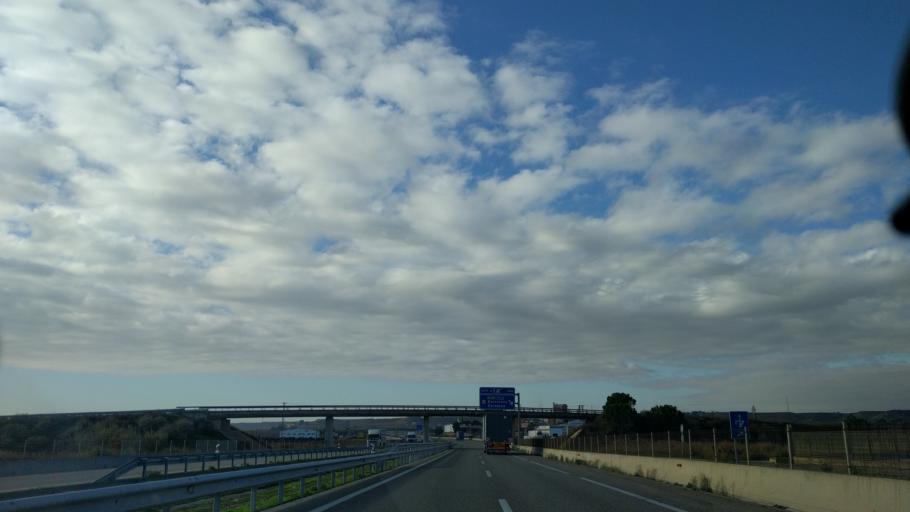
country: ES
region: Catalonia
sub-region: Provincia de Lleida
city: Soses
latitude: 41.5471
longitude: 0.4833
